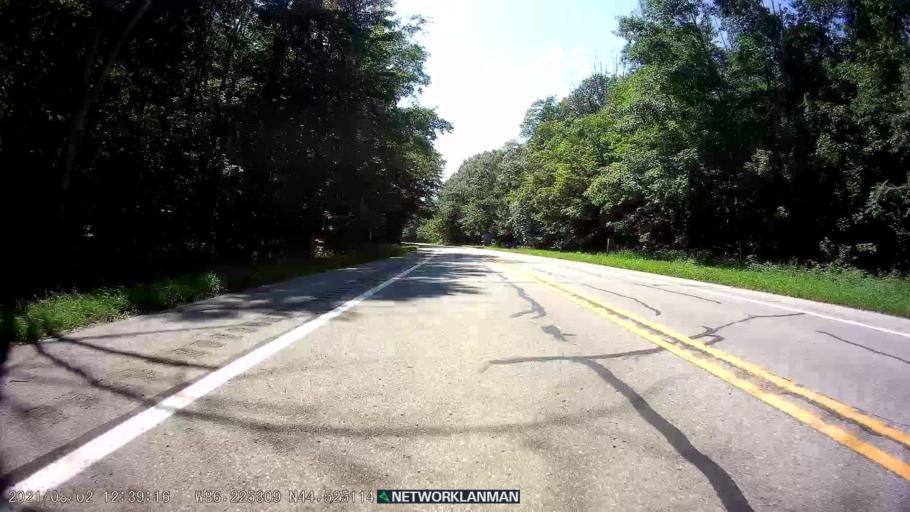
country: US
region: Michigan
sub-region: Benzie County
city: Frankfort
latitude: 44.5252
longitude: -86.2250
